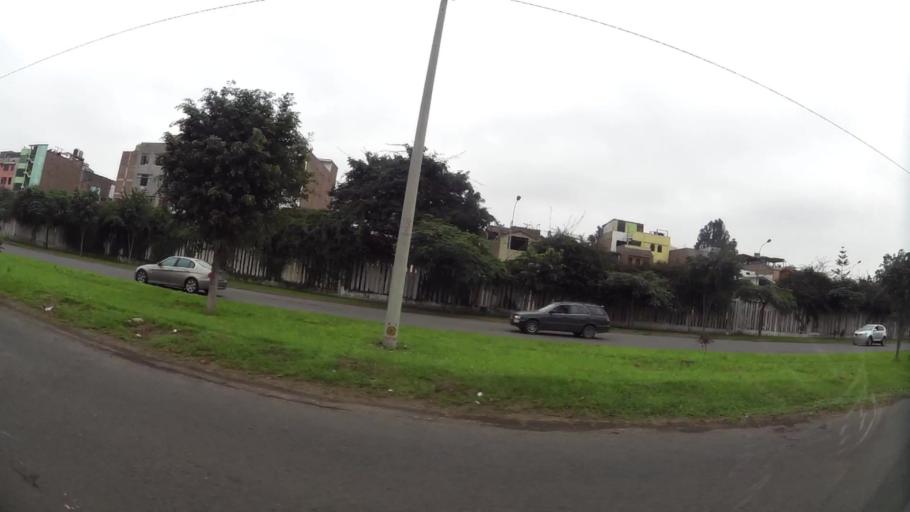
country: PE
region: Lima
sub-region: Lima
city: Vitarte
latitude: -12.0553
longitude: -76.9379
